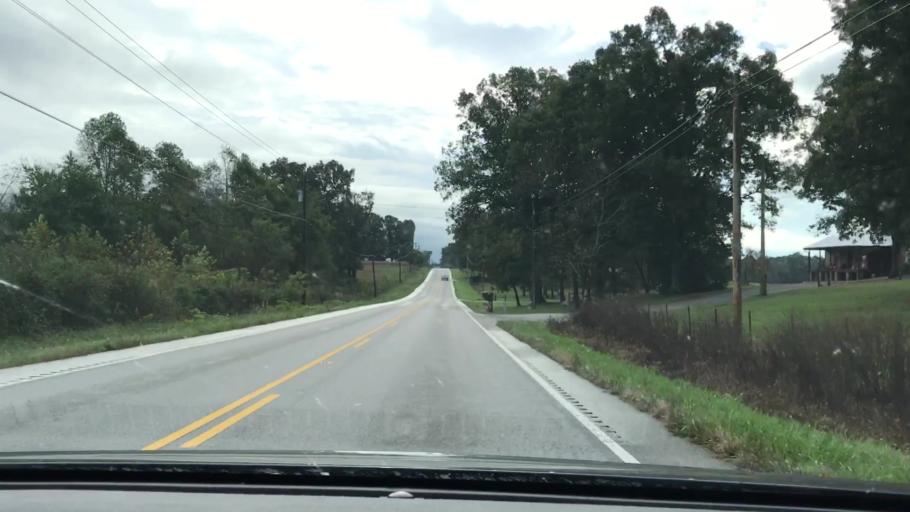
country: US
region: Tennessee
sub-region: Fentress County
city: Jamestown
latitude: 36.3672
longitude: -84.8476
